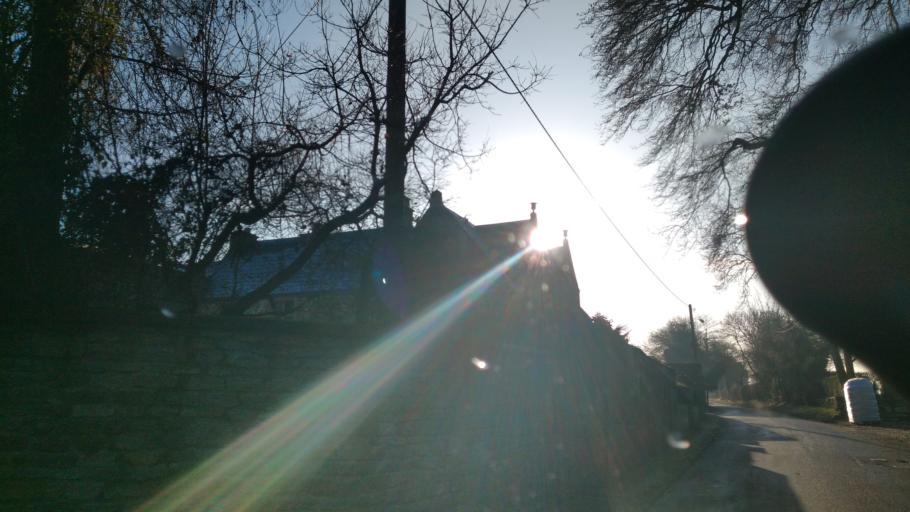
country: GB
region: England
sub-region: Wiltshire
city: Lacock
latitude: 51.4241
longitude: -2.1291
